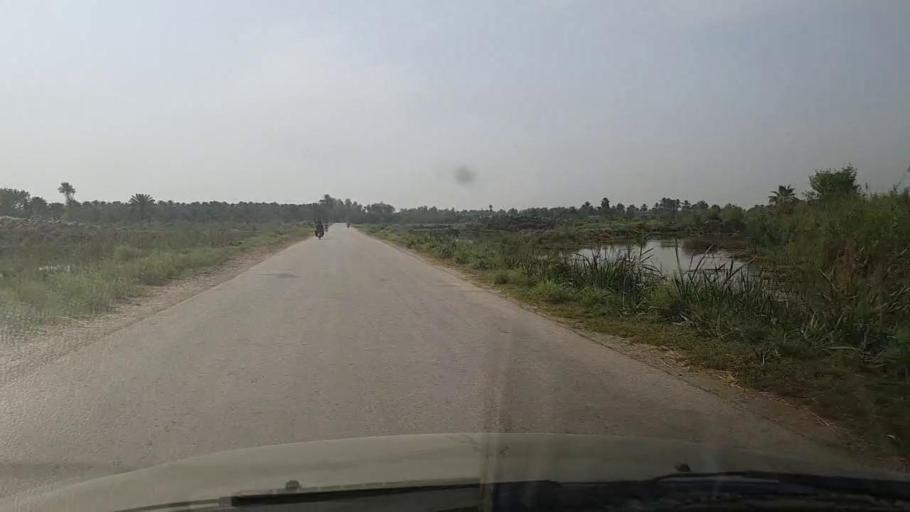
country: PK
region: Sindh
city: Gambat
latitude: 27.4581
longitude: 68.4838
